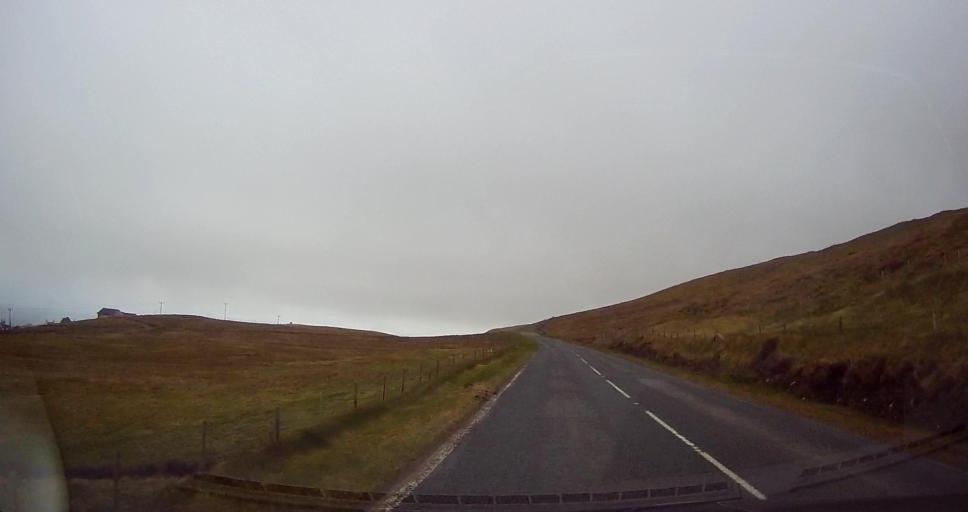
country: GB
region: Scotland
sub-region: Shetland Islands
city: Sandwick
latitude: 59.9703
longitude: -1.2792
